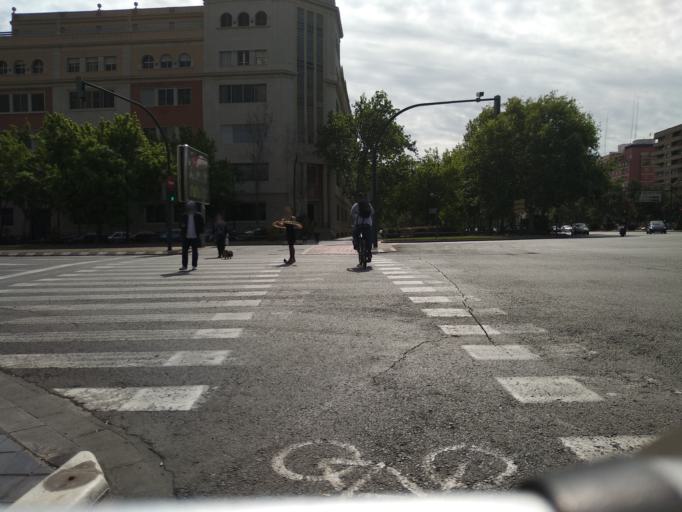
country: ES
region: Valencia
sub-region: Provincia de Valencia
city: Valencia
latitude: 39.4768
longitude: -0.3558
